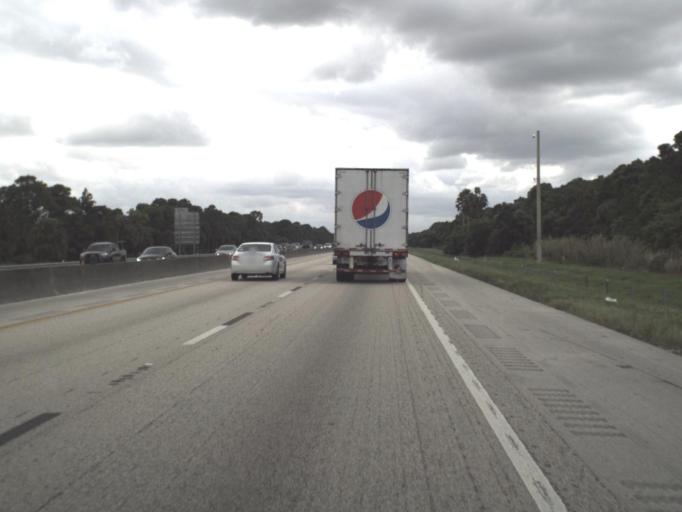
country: US
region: Florida
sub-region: Palm Beach County
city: Palm Beach Gardens
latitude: 26.7850
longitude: -80.1323
